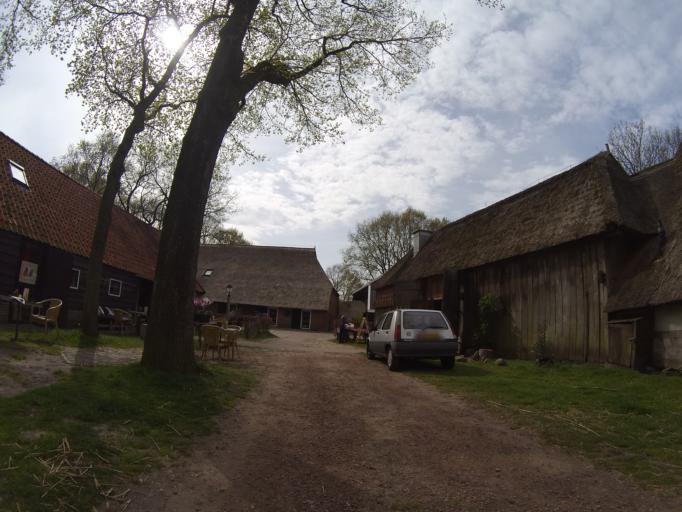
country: NL
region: Drenthe
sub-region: Gemeente Borger-Odoorn
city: Borger
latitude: 52.8441
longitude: 6.6584
